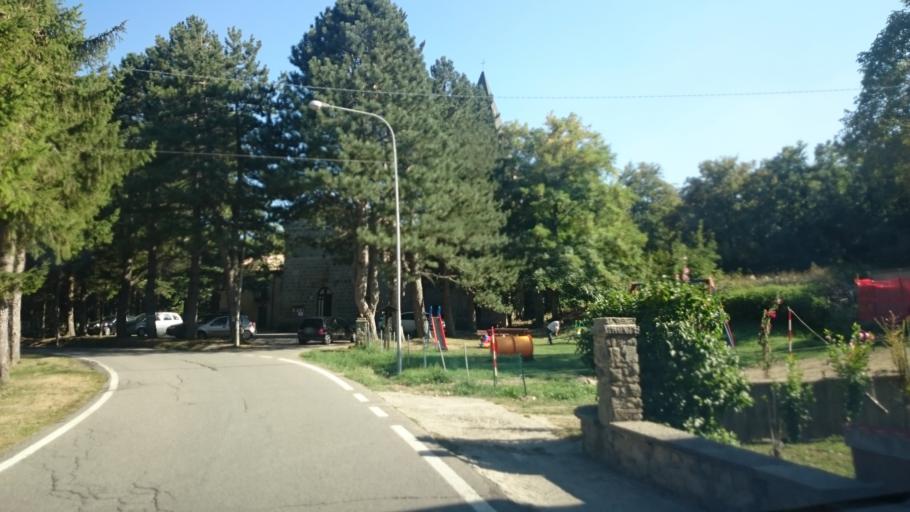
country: IT
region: Emilia-Romagna
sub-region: Provincia di Reggio Emilia
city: Villa Minozzo
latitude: 44.3052
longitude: 10.4333
